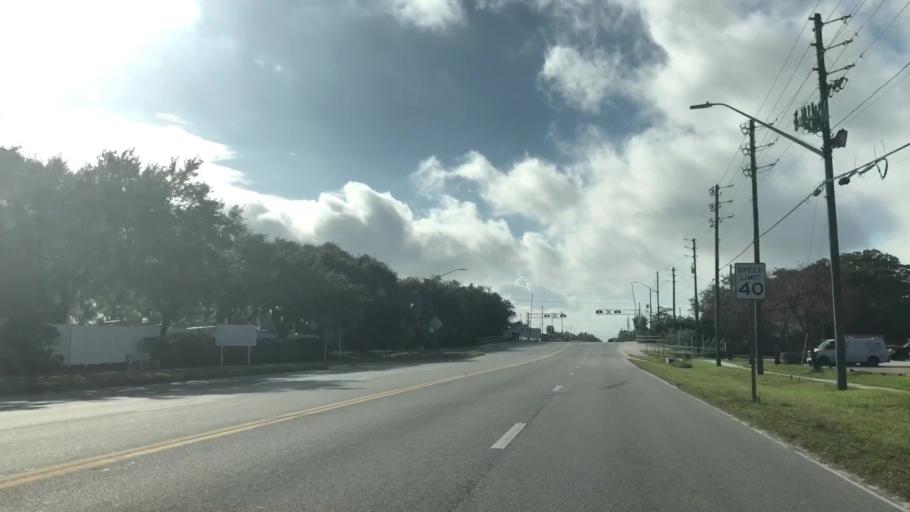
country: US
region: Florida
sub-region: Pinellas County
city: Dunedin
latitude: 27.9835
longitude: -82.7547
